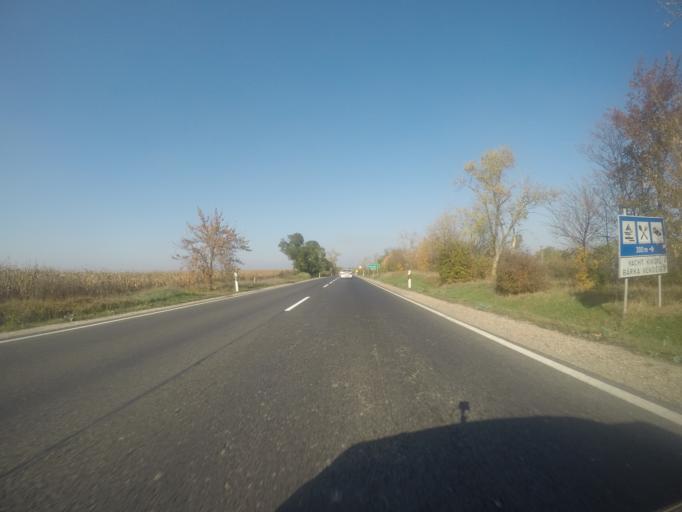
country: HU
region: Fejer
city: Baracs
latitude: 46.8974
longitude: 18.9226
